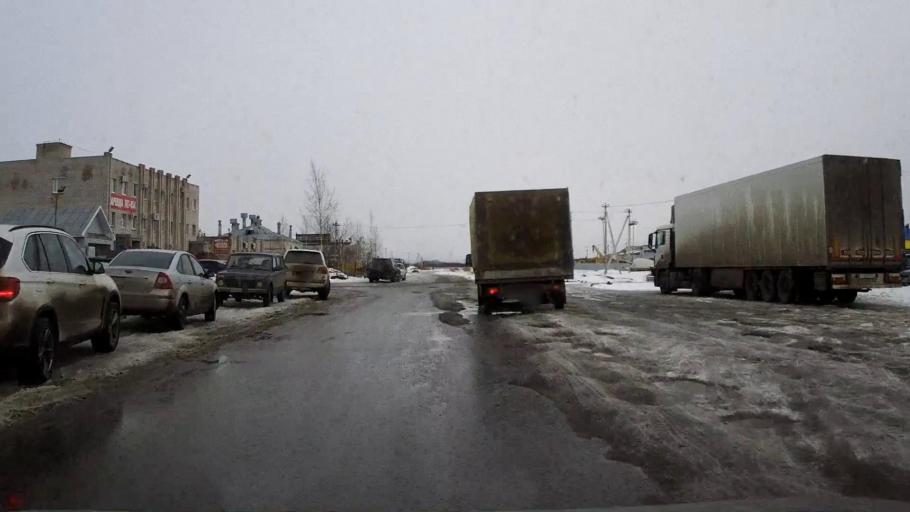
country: RU
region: Vologda
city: Vologda
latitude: 59.2205
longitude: 39.9477
